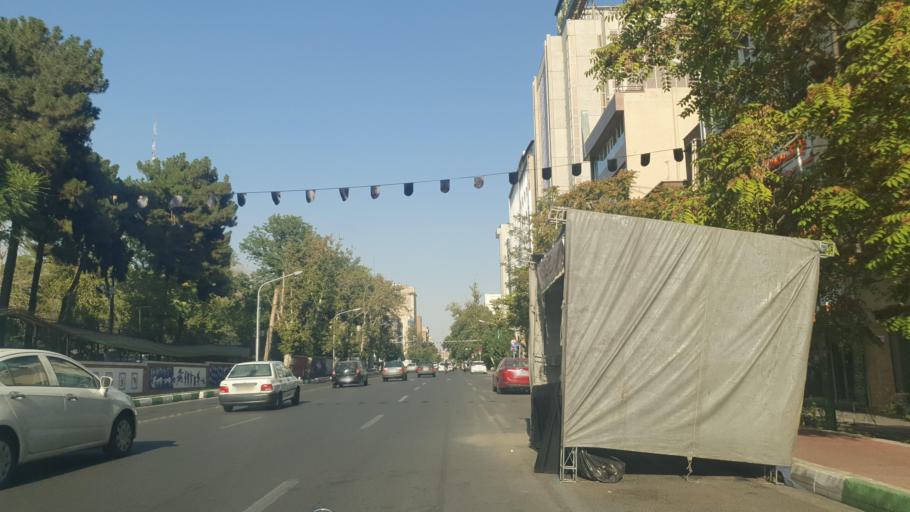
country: IR
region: Tehran
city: Tehran
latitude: 35.7069
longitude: 51.4236
